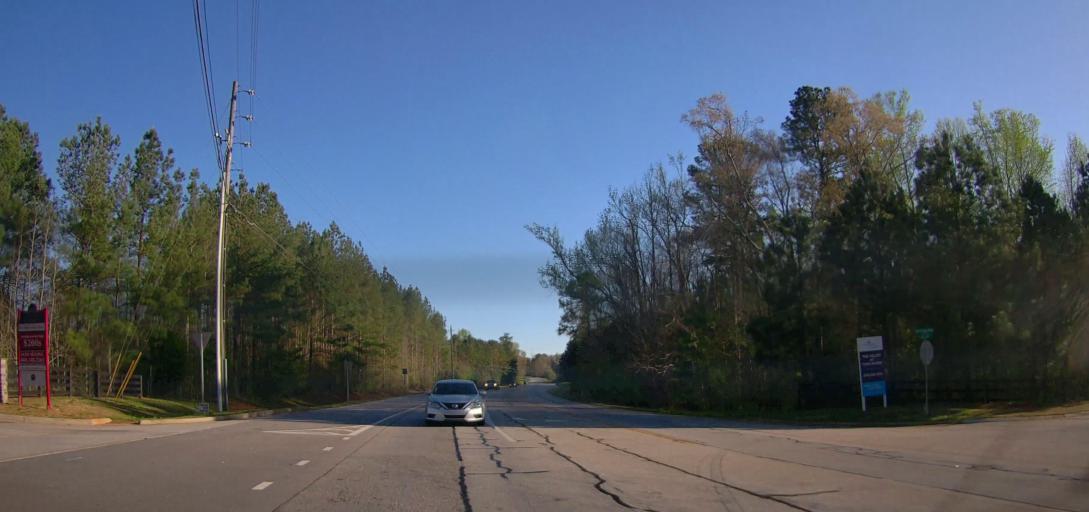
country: US
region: Georgia
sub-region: Newton County
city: Oakwood
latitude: 33.4558
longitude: -83.9035
